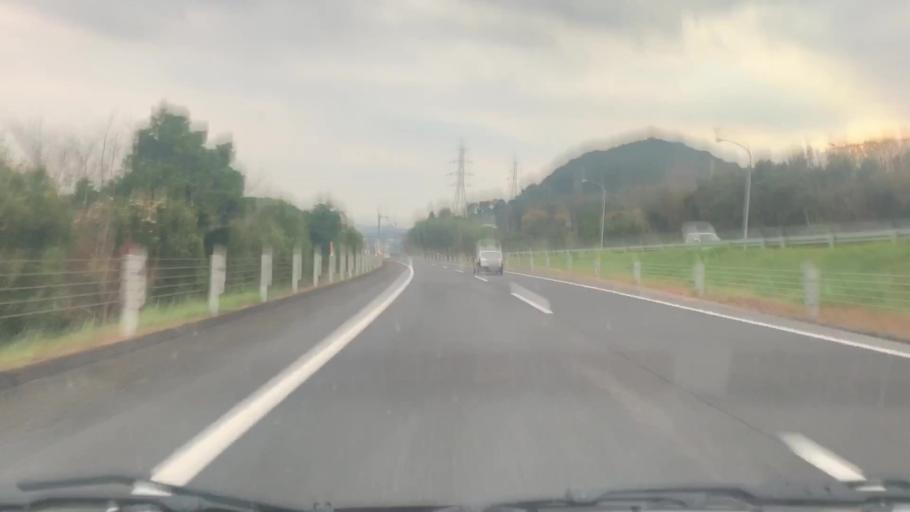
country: JP
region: Nagasaki
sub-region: Isahaya-shi
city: Isahaya
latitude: 32.8603
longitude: 130.0029
